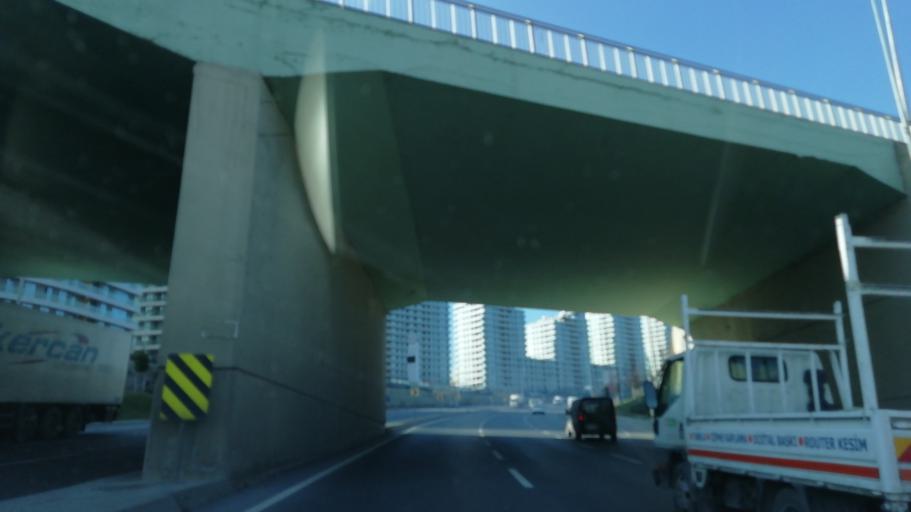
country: TR
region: Istanbul
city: Mahmutbey
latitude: 41.0653
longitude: 28.8450
